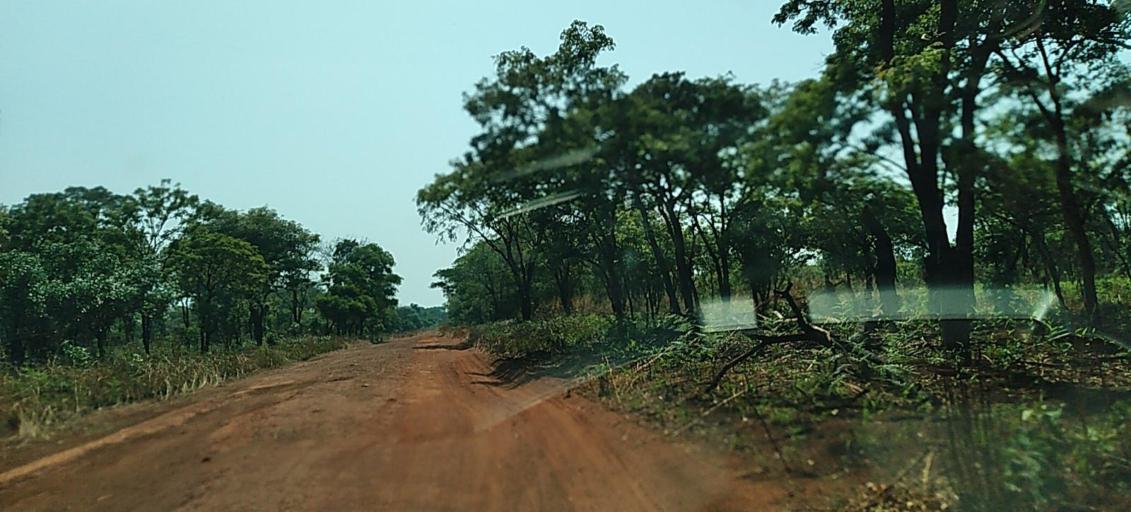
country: ZM
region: North-Western
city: Kansanshi
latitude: -12.0082
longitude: 26.5171
